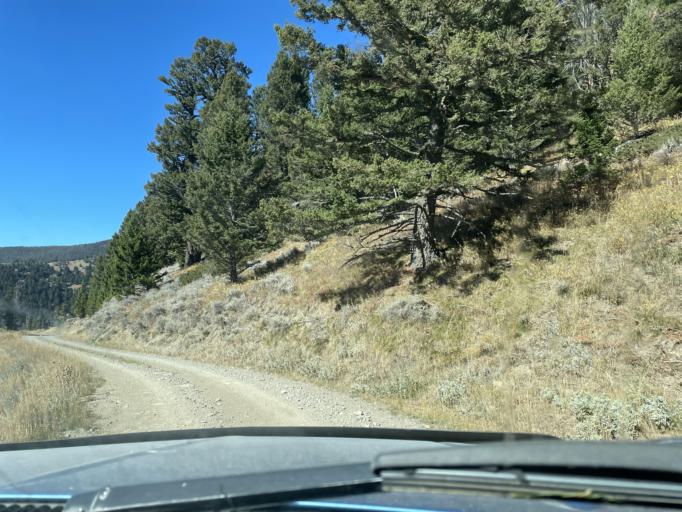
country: US
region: Montana
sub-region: Broadwater County
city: Townsend
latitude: 46.5090
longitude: -111.2834
